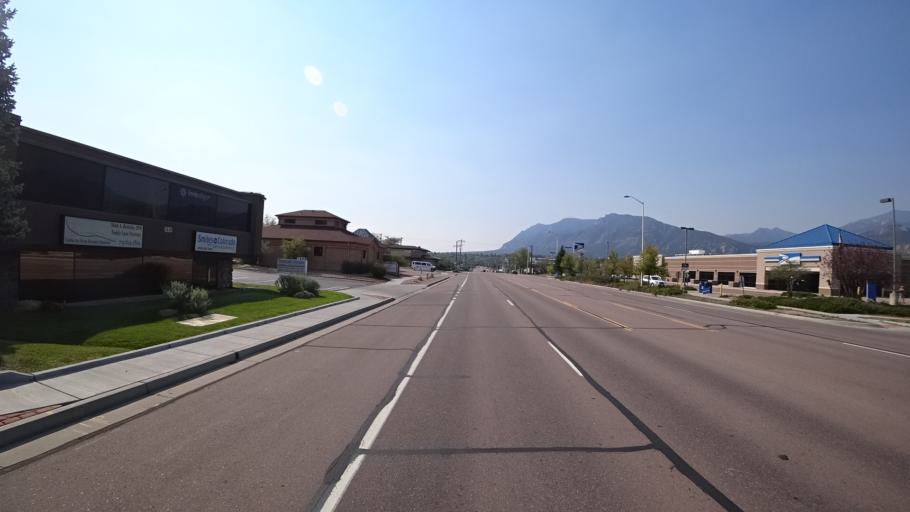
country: US
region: Colorado
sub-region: El Paso County
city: Colorado Springs
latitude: 38.8115
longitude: -104.8408
